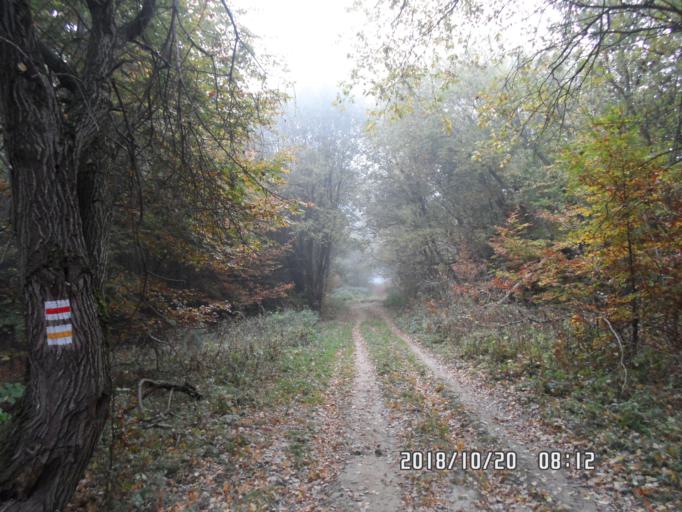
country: HU
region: Veszprem
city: Herend
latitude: 47.2043
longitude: 17.7588
